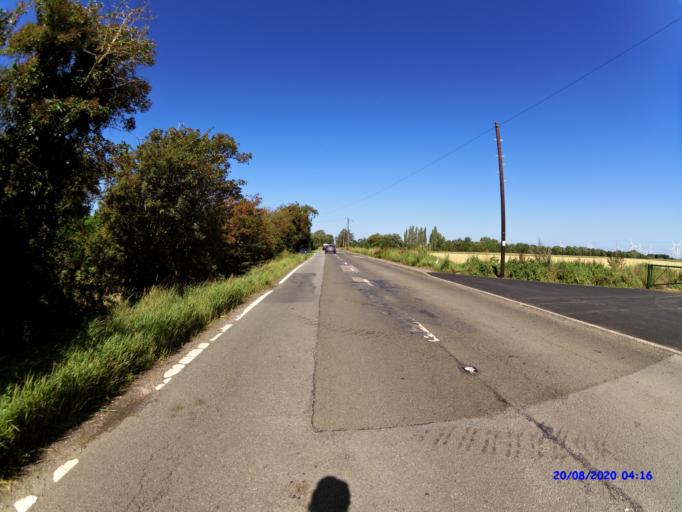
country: GB
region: England
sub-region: Cambridgeshire
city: Ramsey
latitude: 52.4877
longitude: -0.1124
